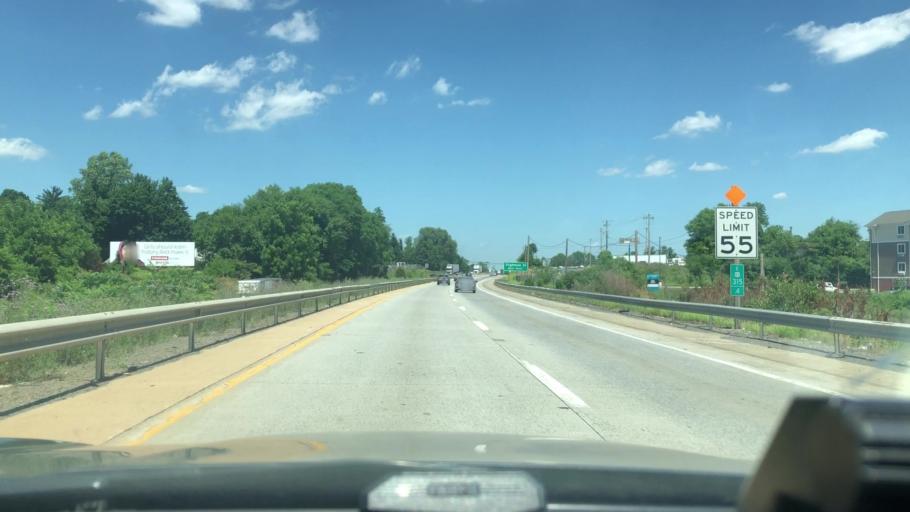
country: US
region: Pennsylvania
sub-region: Lehigh County
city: Wescosville
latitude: 40.5902
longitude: -75.5877
